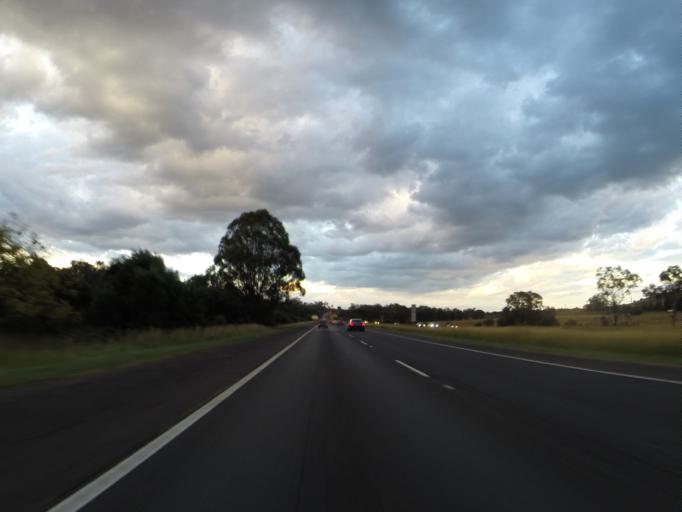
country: AU
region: New South Wales
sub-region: Campbelltown Municipality
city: Glen Alpine
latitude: -34.1005
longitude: 150.7637
